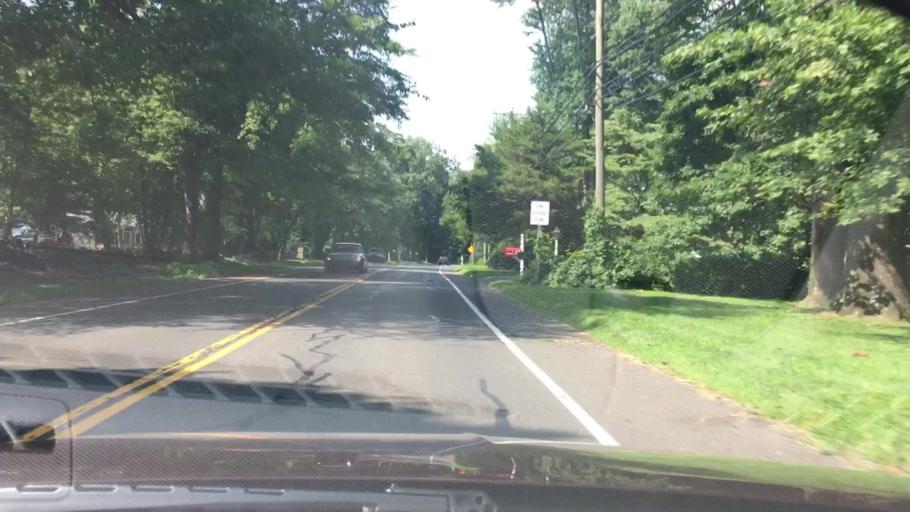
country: US
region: Connecticut
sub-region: Fairfield County
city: Norwalk
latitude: 41.1388
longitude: -73.4167
